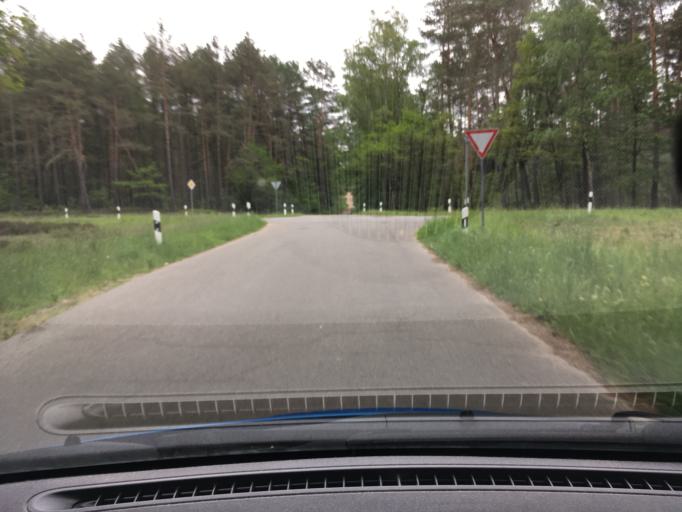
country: DE
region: Lower Saxony
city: Bispingen
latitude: 53.0709
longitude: 10.0190
